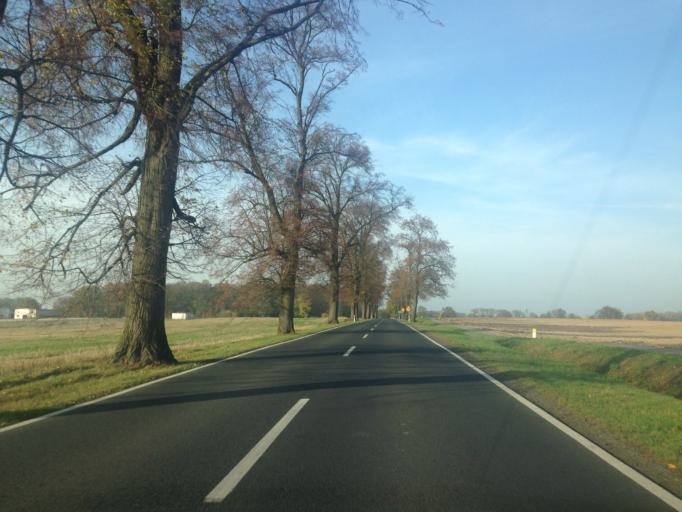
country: PL
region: Kujawsko-Pomorskie
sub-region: Powiat swiecki
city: Pruszcz
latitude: 53.2913
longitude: 18.1205
